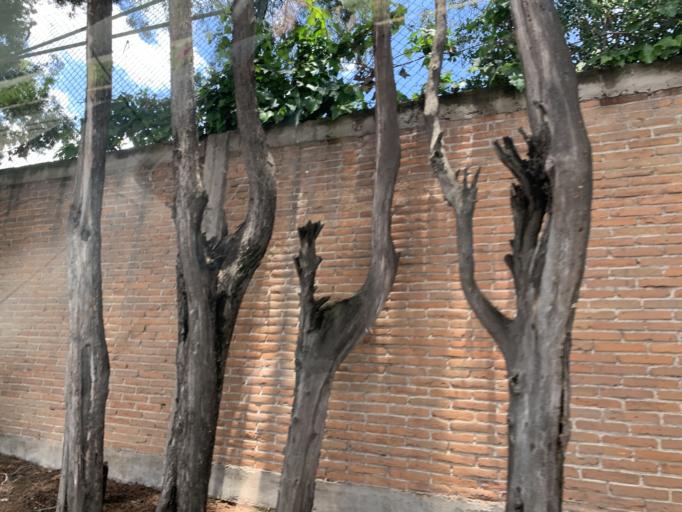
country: MX
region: Puebla
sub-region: Cuautlancingo
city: Sanctorum
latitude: 19.0968
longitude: -98.2316
